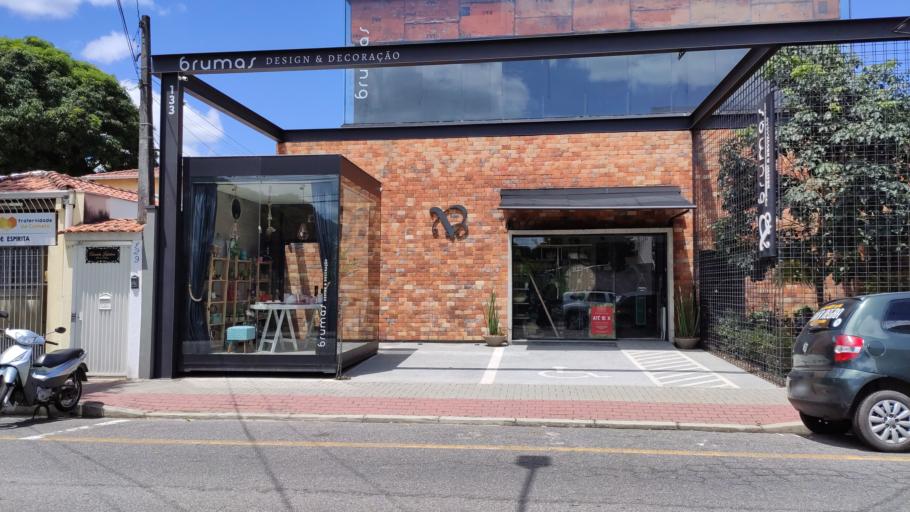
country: BR
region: Sao Paulo
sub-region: Sao Jose Dos Campos
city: Sao Jose dos Campos
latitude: -23.2035
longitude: -45.9018
